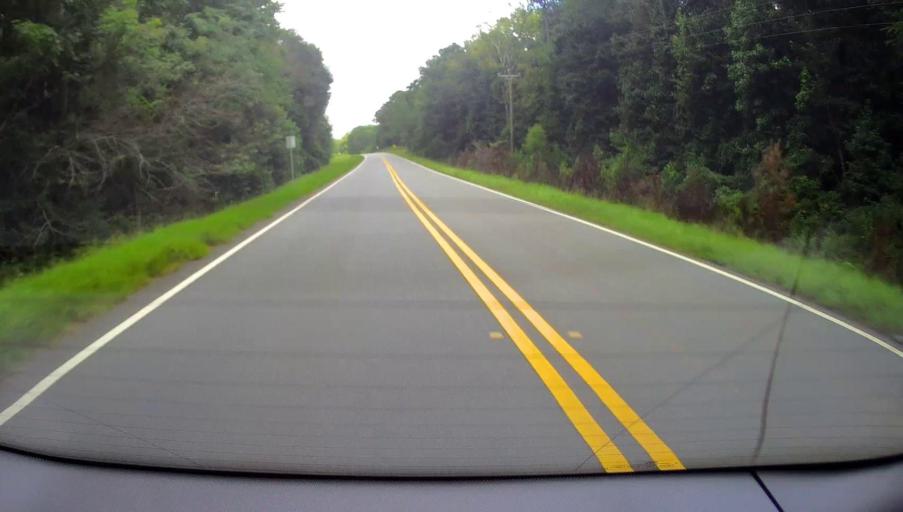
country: US
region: Georgia
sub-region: Bibb County
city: West Point
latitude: 32.8653
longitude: -83.8713
